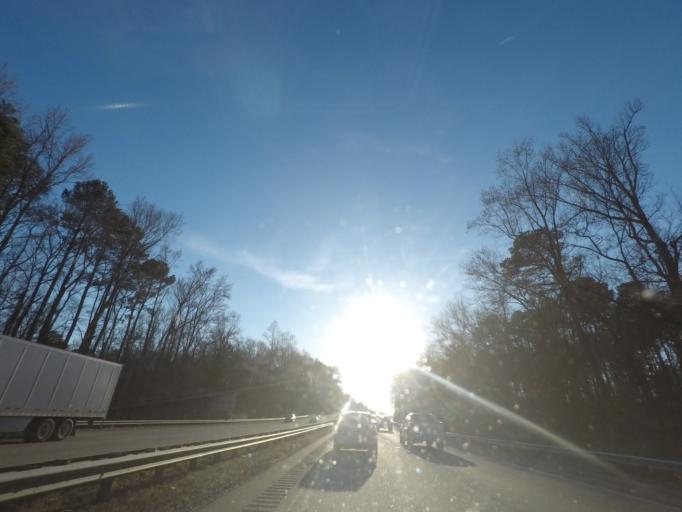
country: US
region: North Carolina
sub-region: Durham County
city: Gorman
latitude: 36.0216
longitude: -78.8554
